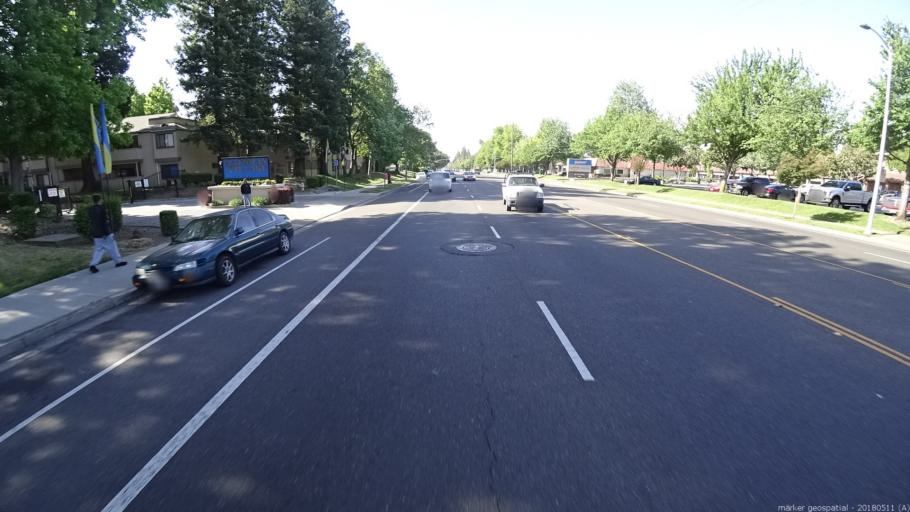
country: US
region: California
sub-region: Sacramento County
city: Sacramento
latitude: 38.6262
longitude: -121.4979
